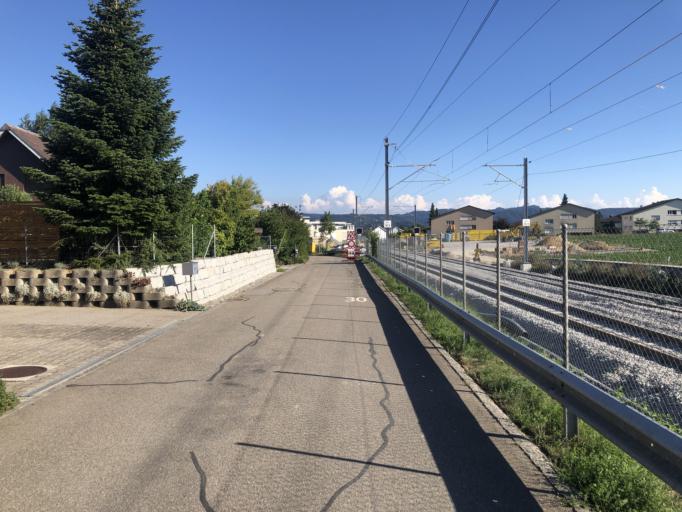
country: CH
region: Bern
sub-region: Bern-Mittelland District
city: Jegenstorf
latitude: 47.0574
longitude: 7.5095
